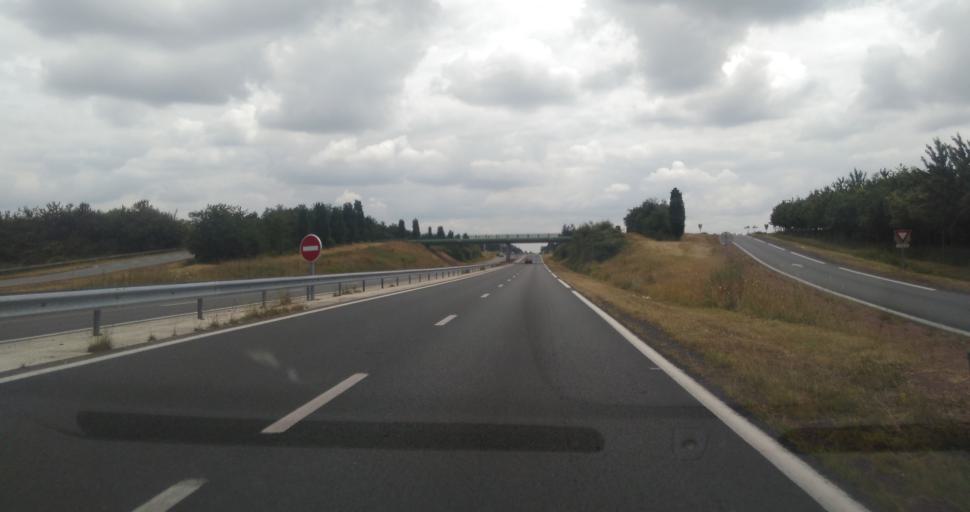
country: FR
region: Pays de la Loire
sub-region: Departement de la Vendee
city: La Chaize-le-Vicomte
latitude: 46.6538
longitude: -1.2331
